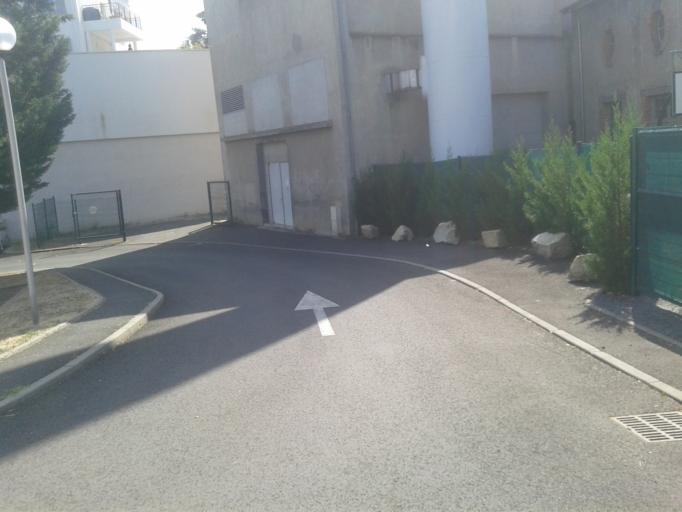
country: FR
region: Auvergne
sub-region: Departement du Puy-de-Dome
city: Chamalieres
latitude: 45.7695
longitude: 3.0584
